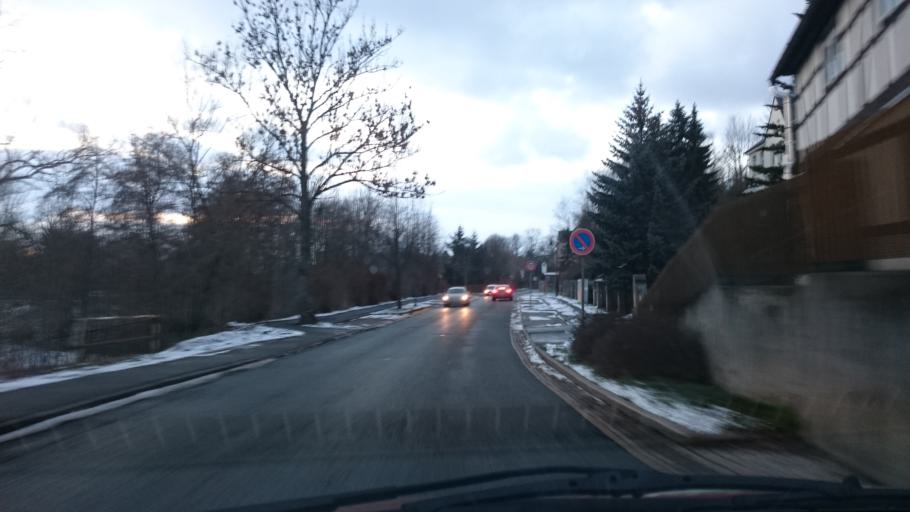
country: DE
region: Saxony
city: Reinsdorf
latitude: 50.7044
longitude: 12.5432
